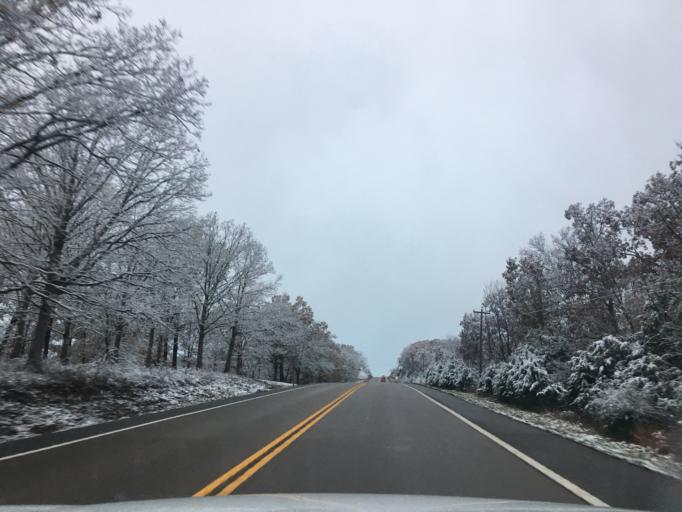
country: US
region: Missouri
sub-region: Osage County
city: Linn
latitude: 38.4713
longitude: -91.7798
